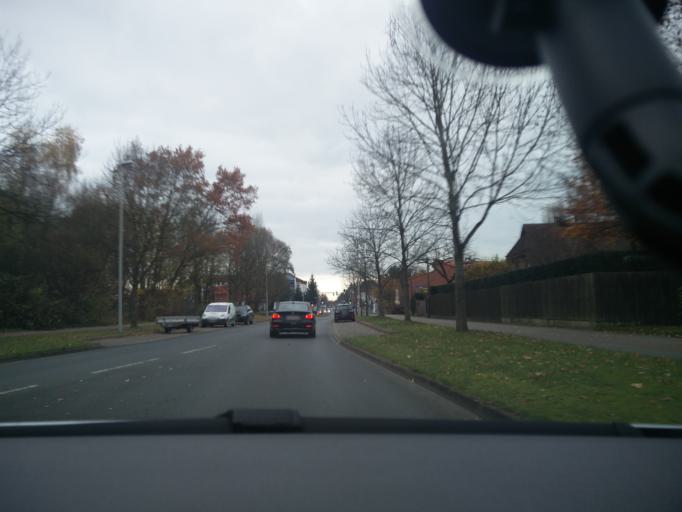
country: DE
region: Lower Saxony
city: Laatzen
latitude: 52.3441
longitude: 9.8213
